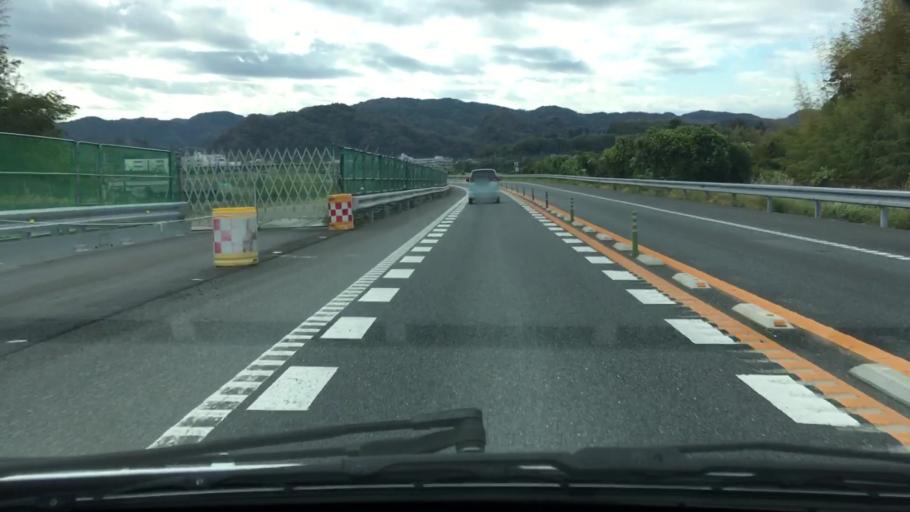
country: JP
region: Chiba
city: Kimitsu
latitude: 35.2264
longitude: 139.8857
